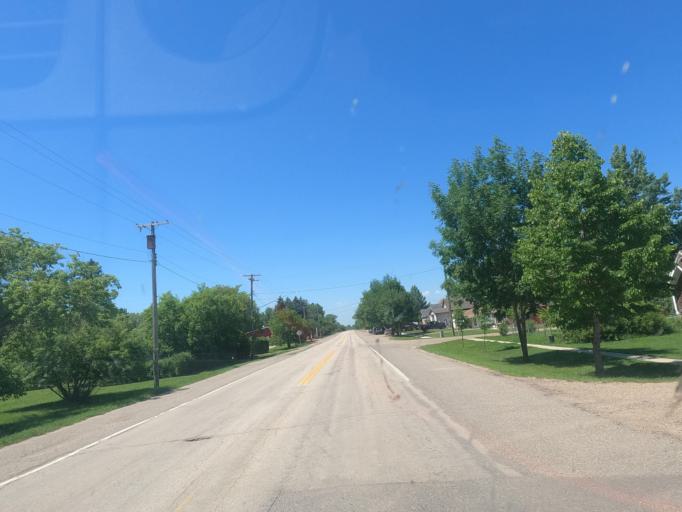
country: CA
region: Manitoba
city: Souris
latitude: 49.6209
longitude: -100.2667
